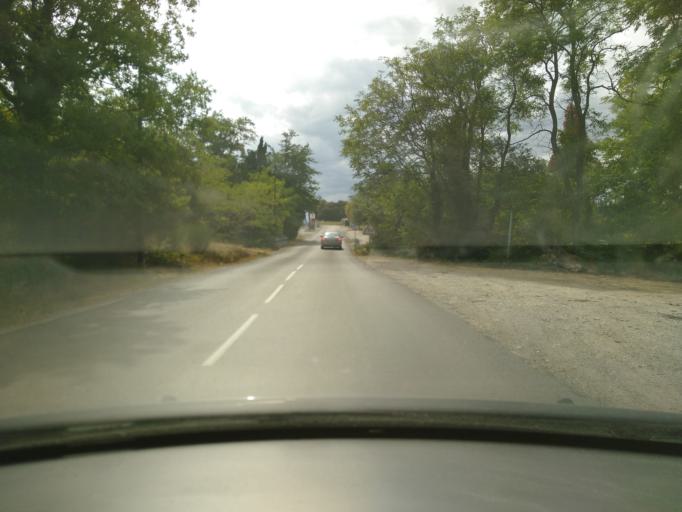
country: FR
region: Rhone-Alpes
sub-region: Departement de la Drome
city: Taulignan
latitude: 44.4383
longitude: 5.0184
